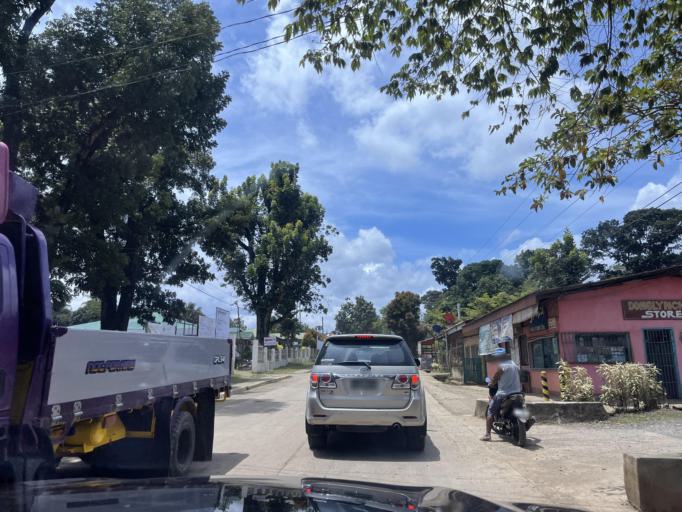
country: PH
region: Northern Mindanao
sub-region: Province of Bukidnon
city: Kisolon
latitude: 8.3263
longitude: 124.9770
